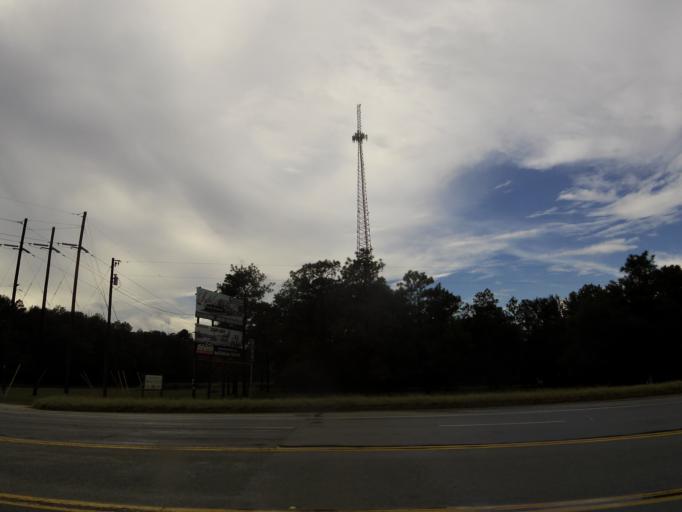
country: US
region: Georgia
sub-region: Wayne County
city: Jesup
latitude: 31.6598
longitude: -81.8493
